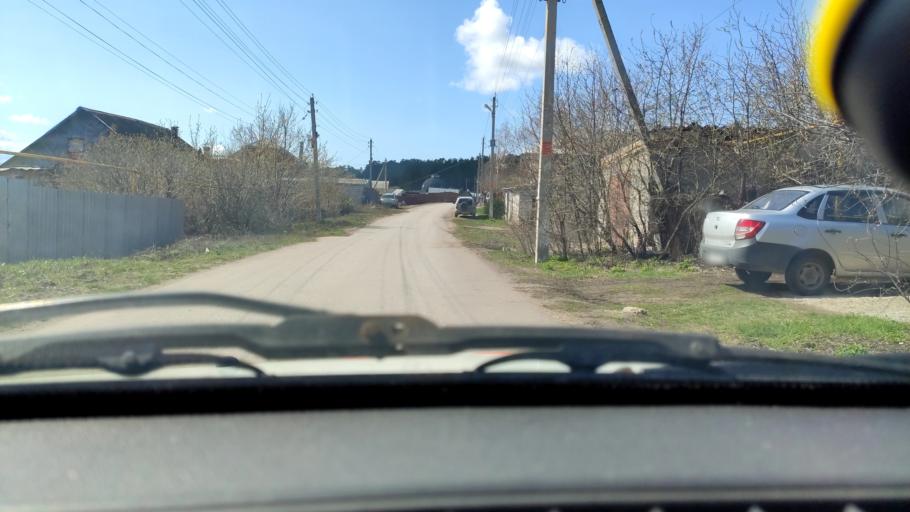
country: RU
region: Samara
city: Zhigulevsk
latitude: 53.5421
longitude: 49.5216
